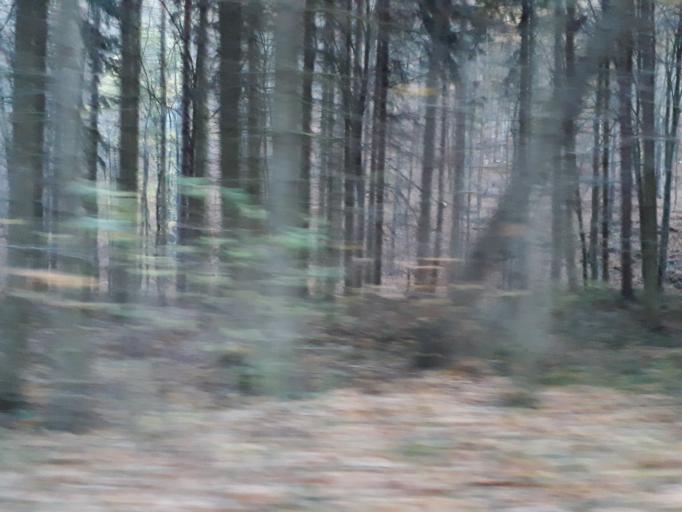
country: DE
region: Saxony
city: Kreischa
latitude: 50.9238
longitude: 13.7786
